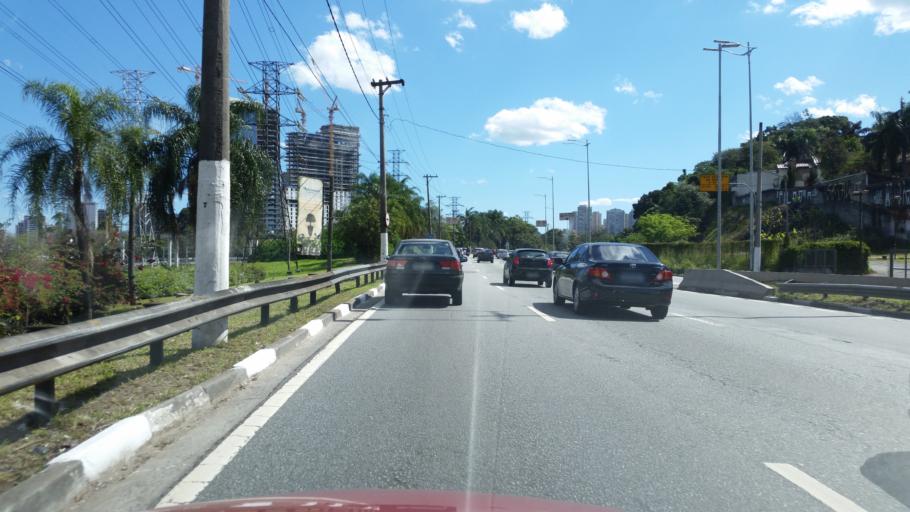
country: BR
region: Sao Paulo
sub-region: Taboao Da Serra
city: Taboao da Serra
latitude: -23.6204
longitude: -46.7027
